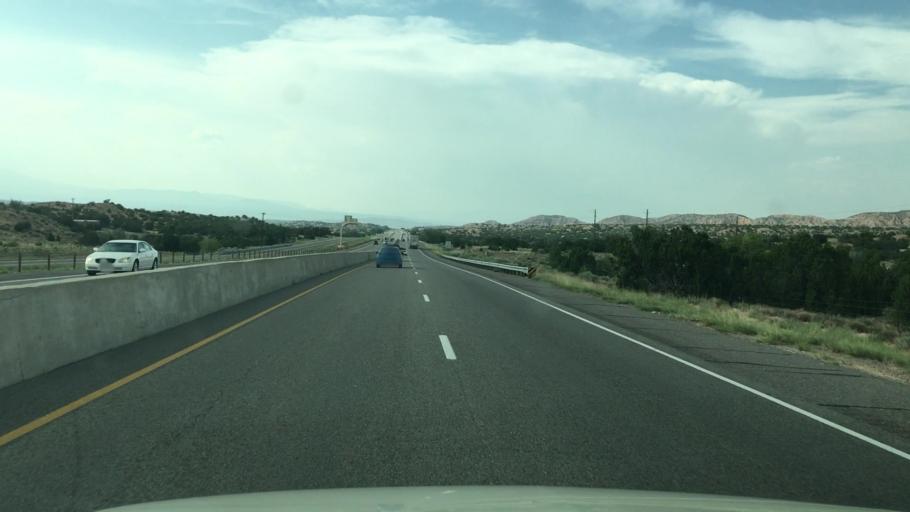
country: US
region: New Mexico
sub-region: Santa Fe County
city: Santa Fe
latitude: 35.7914
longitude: -105.9530
